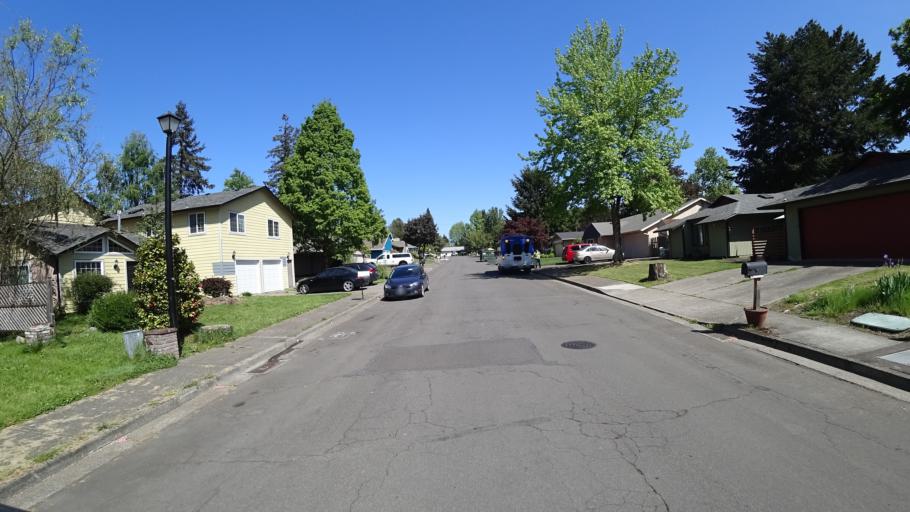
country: US
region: Oregon
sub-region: Washington County
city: Aloha
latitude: 45.4792
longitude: -122.8439
